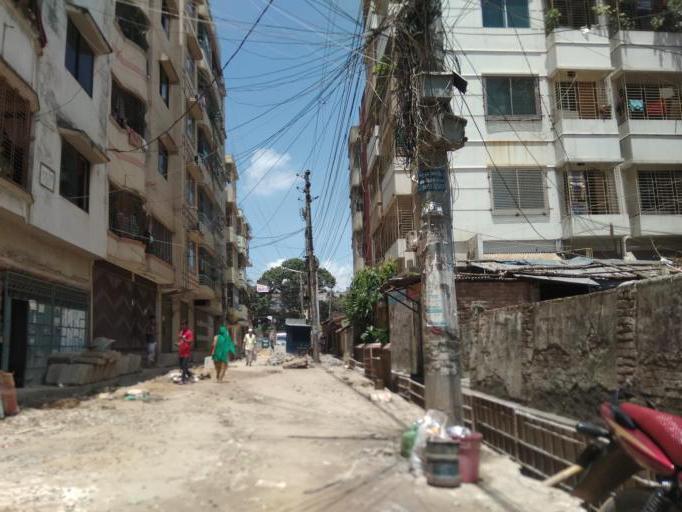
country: BD
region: Dhaka
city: Tungi
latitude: 23.8290
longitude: 90.3665
